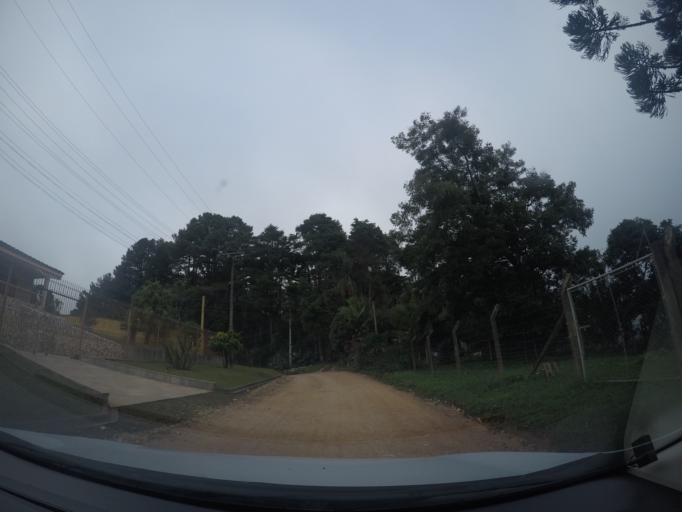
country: BR
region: Parana
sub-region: Colombo
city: Colombo
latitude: -25.3036
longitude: -49.2417
